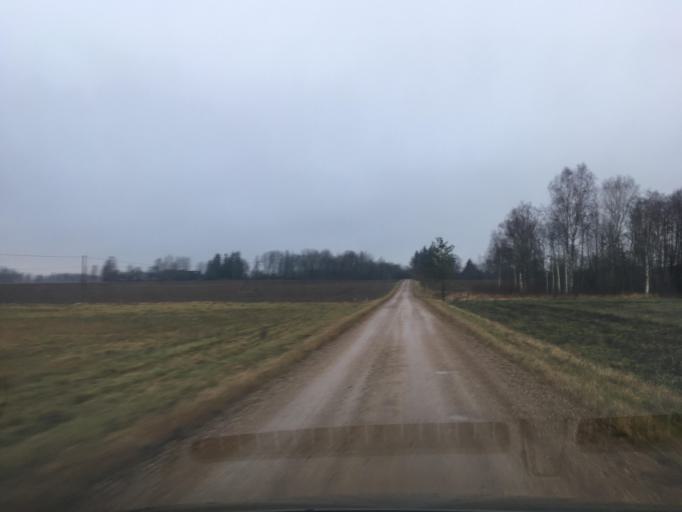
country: EE
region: Tartu
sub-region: Alatskivi vald
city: Kallaste
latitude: 58.3905
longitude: 27.0251
